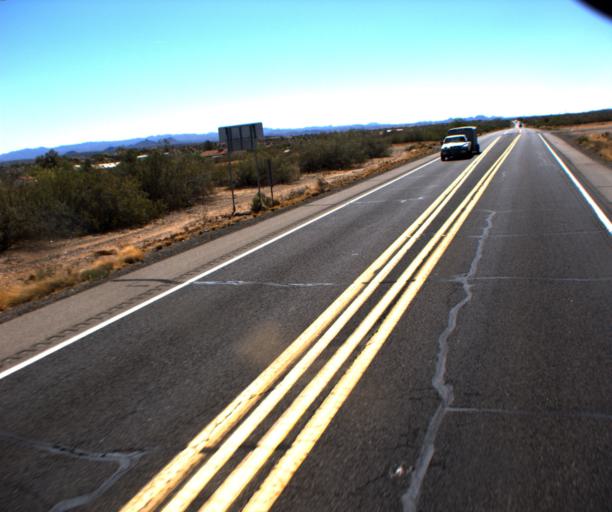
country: US
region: Arizona
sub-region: Maricopa County
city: Wickenburg
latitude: 34.0389
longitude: -112.8293
